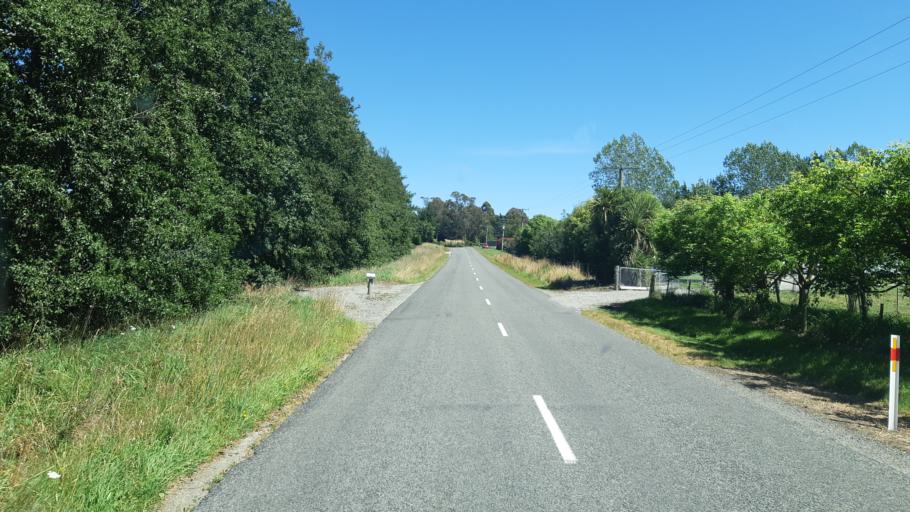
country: NZ
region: Canterbury
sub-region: Timaru District
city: Timaru
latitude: -44.4068
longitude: 171.1418
